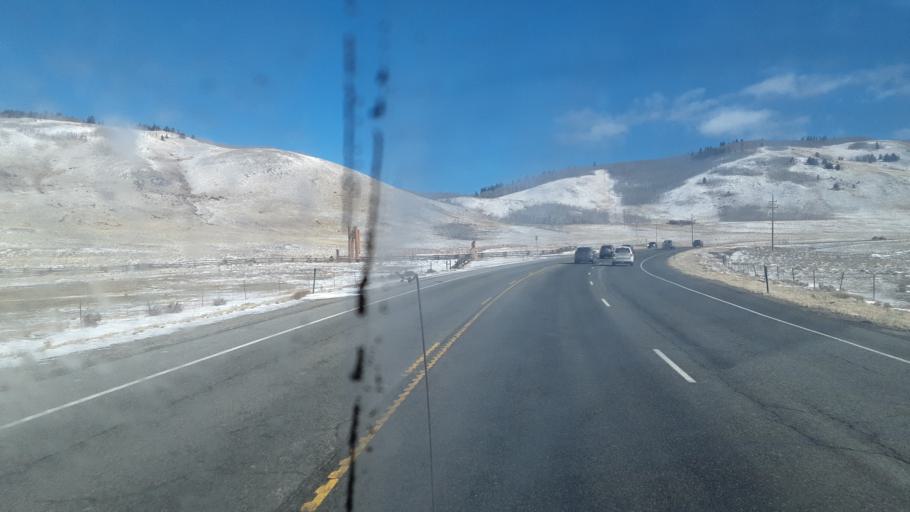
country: US
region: Colorado
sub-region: Summit County
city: Breckenridge
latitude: 39.4065
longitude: -105.7783
